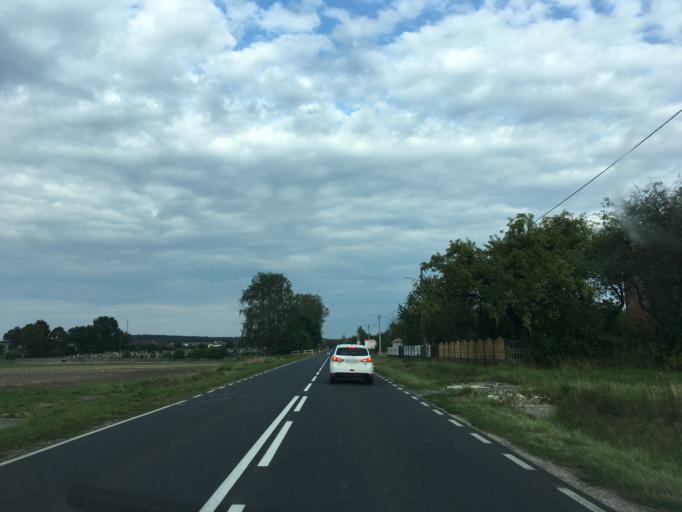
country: PL
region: Swietokrzyskie
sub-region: Powiat wloszczowski
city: Wloszczowa
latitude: 50.8054
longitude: 19.9187
